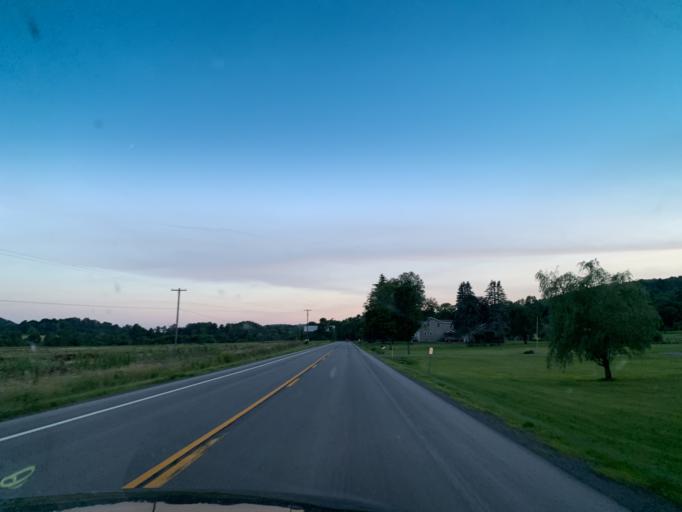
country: US
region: New York
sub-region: Chenango County
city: New Berlin
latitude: 42.7579
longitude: -75.2860
